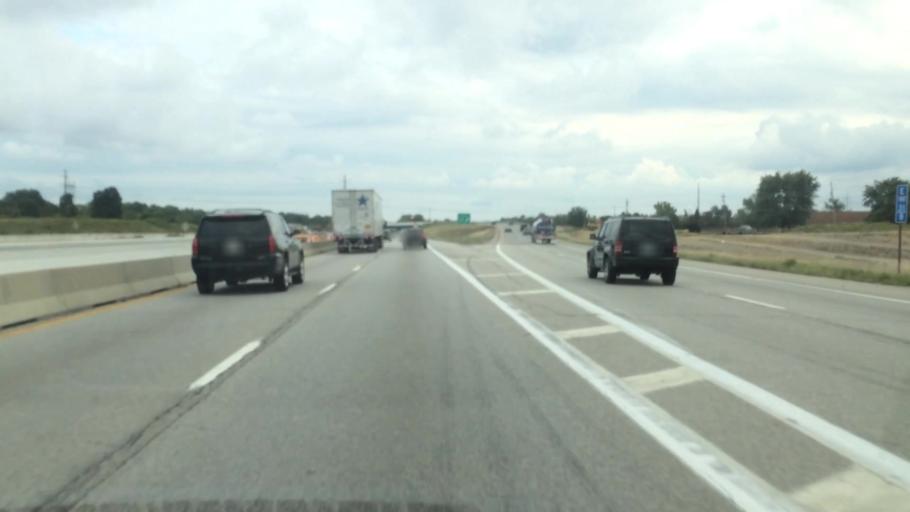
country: US
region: Ohio
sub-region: Cuyahoga County
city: Oakwood
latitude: 41.3576
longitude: -81.5144
